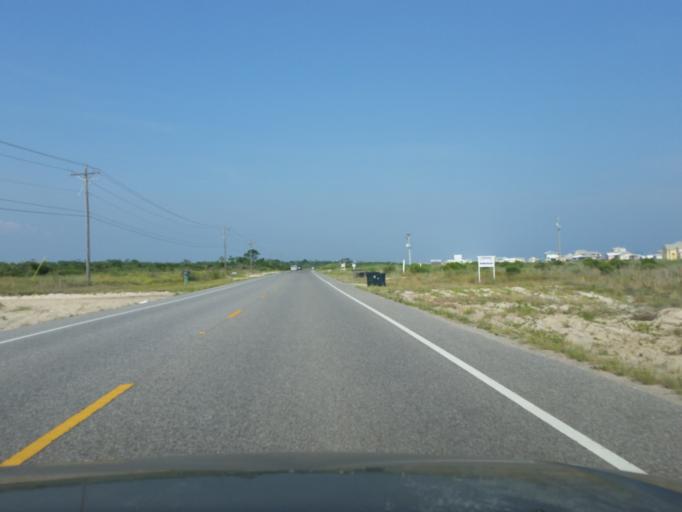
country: US
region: Alabama
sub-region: Mobile County
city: Dauphin Island
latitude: 30.2328
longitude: -87.9623
